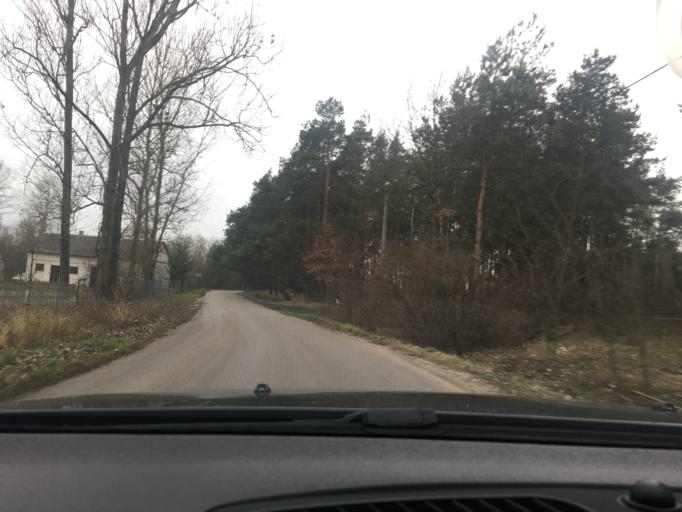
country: PL
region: Swietokrzyskie
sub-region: Powiat jedrzejowski
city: Imielno
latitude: 50.6411
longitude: 20.4155
